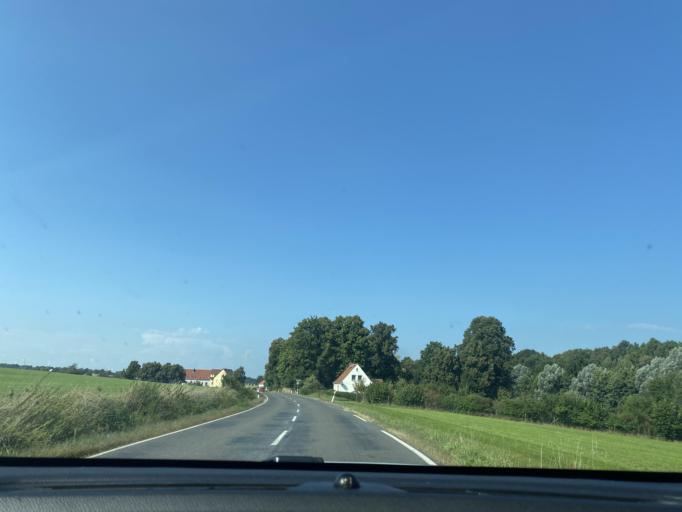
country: DE
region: Saxony
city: Reichenbach
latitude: 51.1683
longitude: 14.7837
